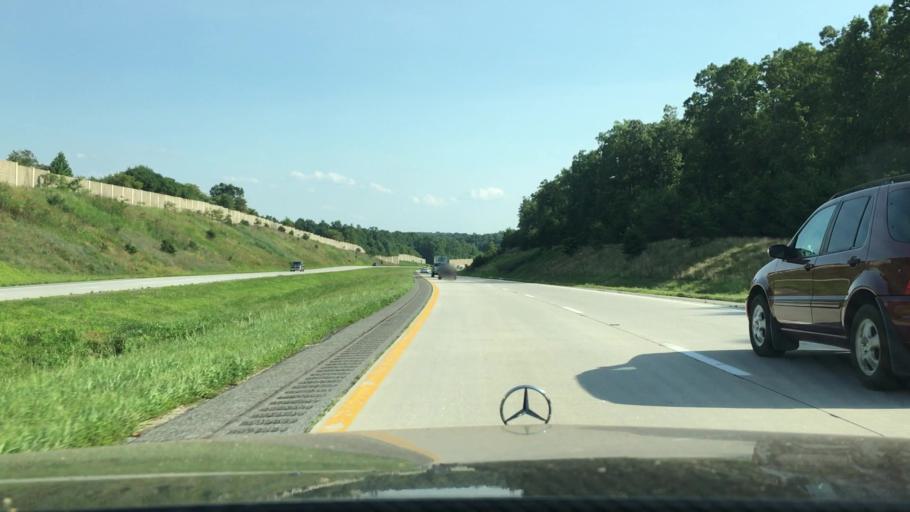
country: US
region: Virginia
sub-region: Amherst County
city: Madison Heights
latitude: 37.4858
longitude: -79.0746
